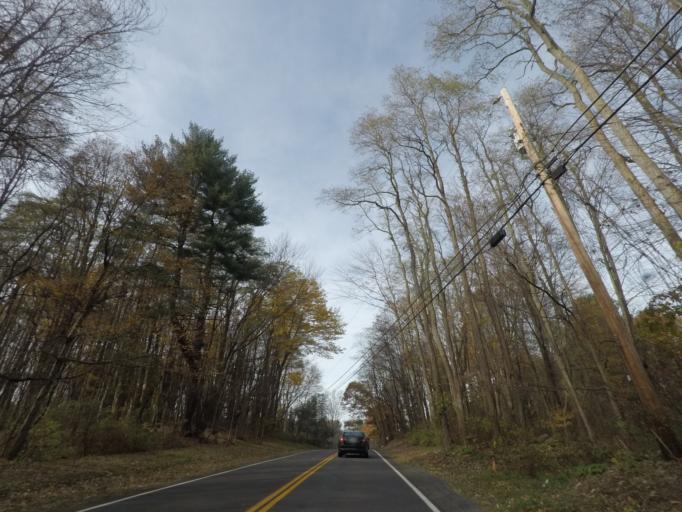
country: US
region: New York
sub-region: Albany County
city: Westmere
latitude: 42.7295
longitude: -73.9006
